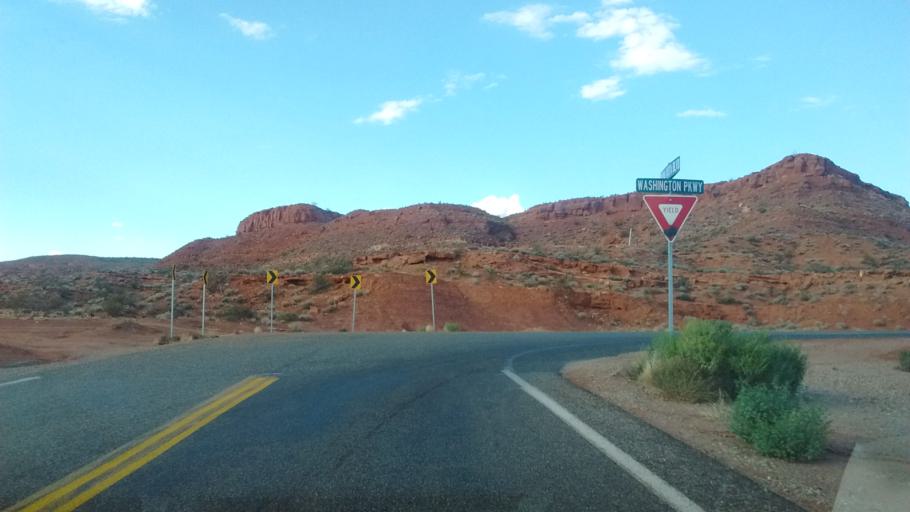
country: US
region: Utah
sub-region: Washington County
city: Washington
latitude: 37.1494
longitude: -113.4922
